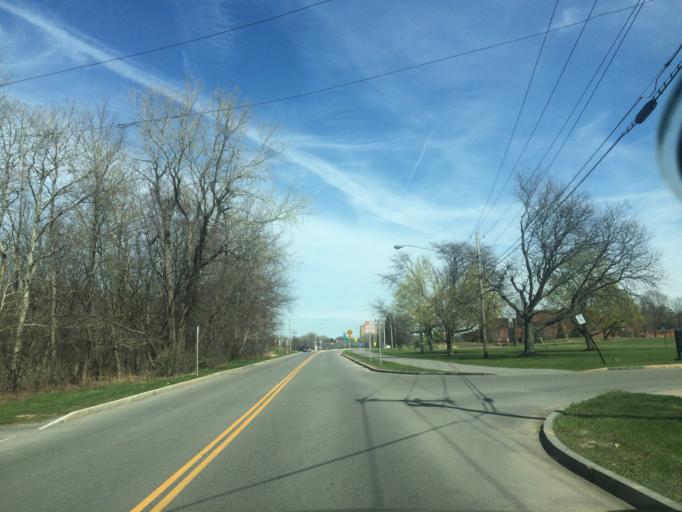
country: US
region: New York
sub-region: Monroe County
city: Rochester
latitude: 43.1140
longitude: -77.6371
